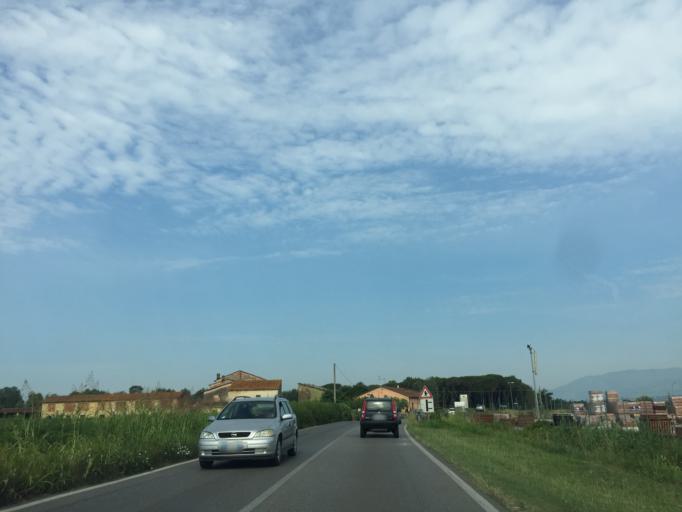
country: IT
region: Tuscany
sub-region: Provincia di Pistoia
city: Monsummano Terme
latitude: 43.8524
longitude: 10.7869
